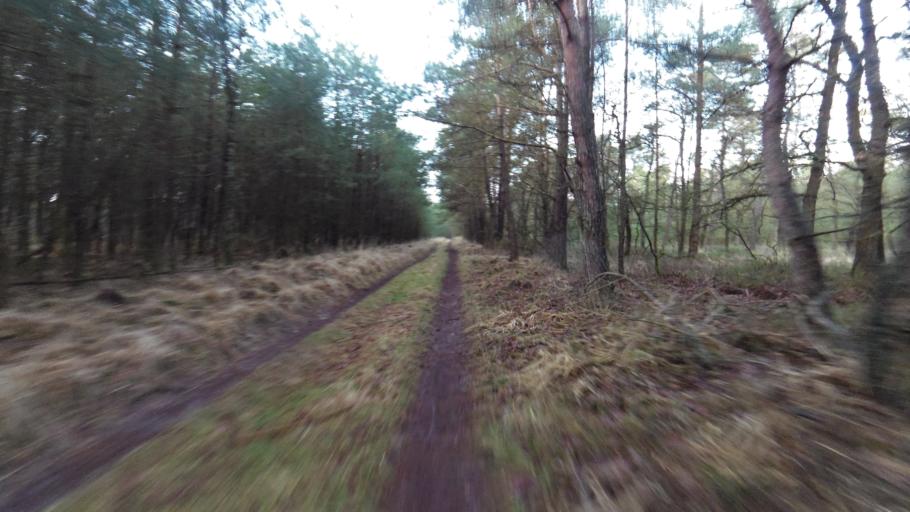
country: NL
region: Gelderland
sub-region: Gemeente Apeldoorn
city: Uddel
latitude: 52.2978
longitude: 5.8423
